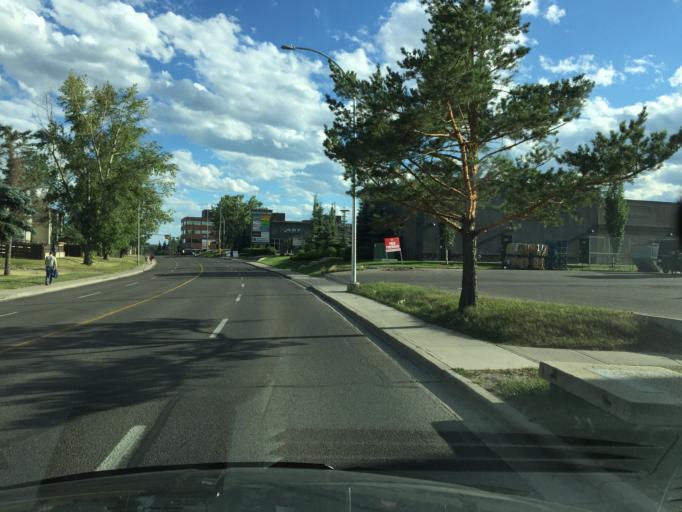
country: CA
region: Alberta
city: Calgary
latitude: 50.9627
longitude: -114.0687
